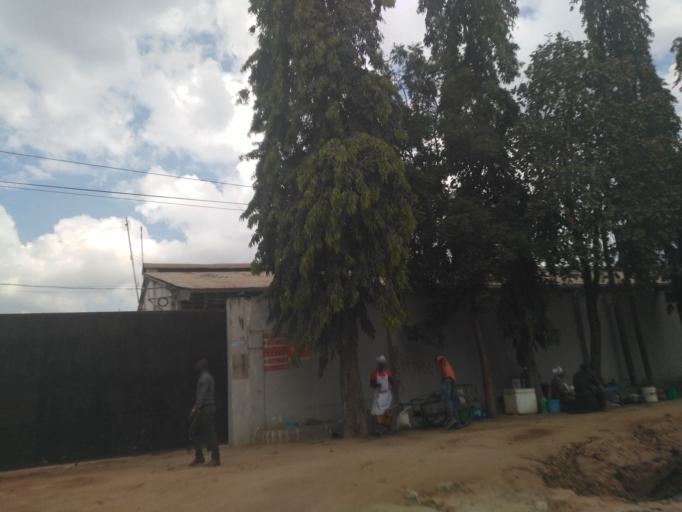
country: TZ
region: Dar es Salaam
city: Dar es Salaam
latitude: -6.8438
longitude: 39.2484
